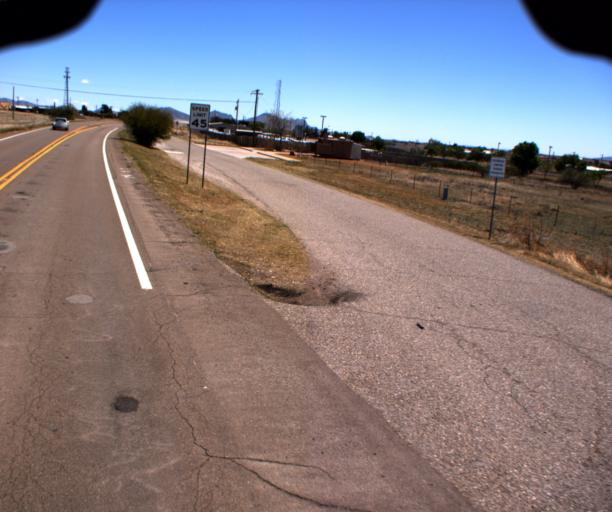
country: US
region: Arizona
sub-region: Pima County
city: Corona de Tucson
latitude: 31.6784
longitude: -110.6611
